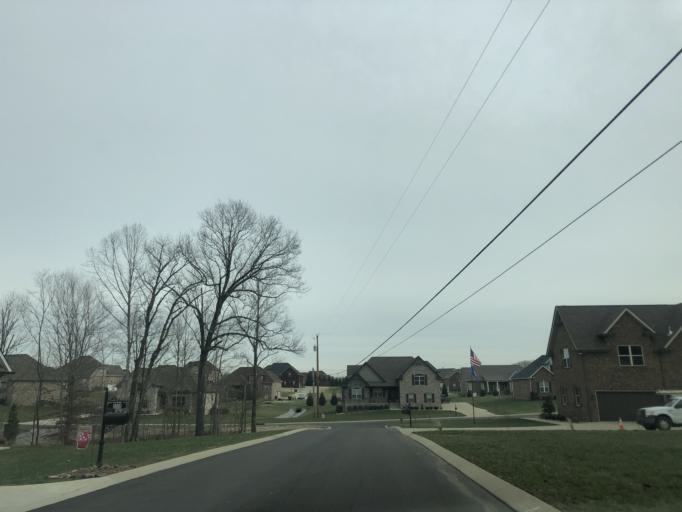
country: US
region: Tennessee
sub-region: Robertson County
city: Greenbrier
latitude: 36.4016
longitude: -86.8216
